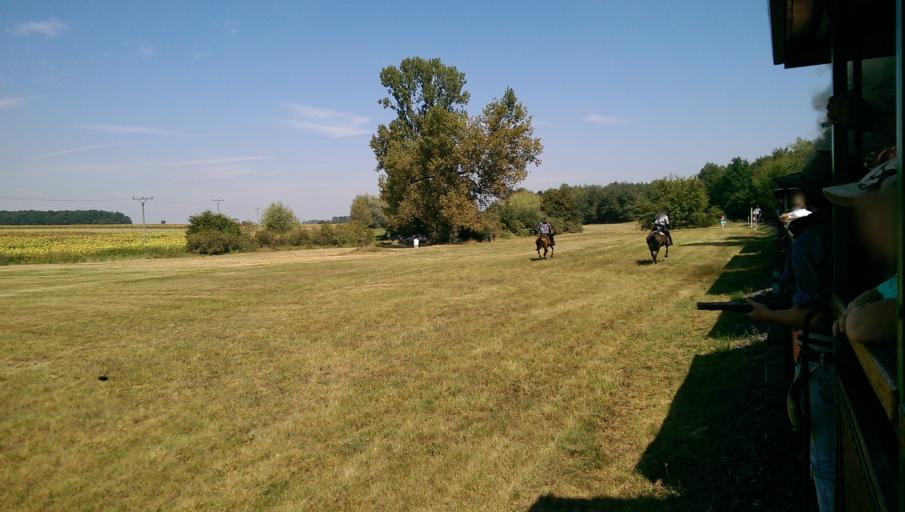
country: CZ
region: Central Bohemia
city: Stary Kolin
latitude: 50.0571
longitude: 15.2663
